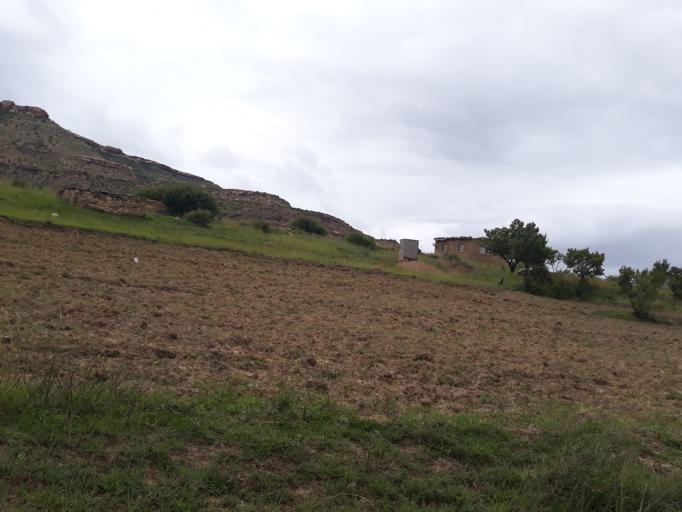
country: LS
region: Quthing
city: Quthing
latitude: -30.3317
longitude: 27.5308
